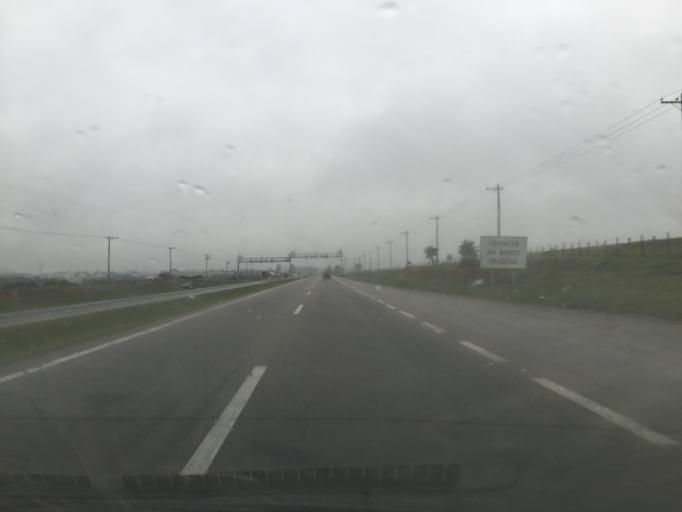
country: BR
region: Sao Paulo
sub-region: Itu
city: Itu
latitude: -23.2931
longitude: -47.3308
